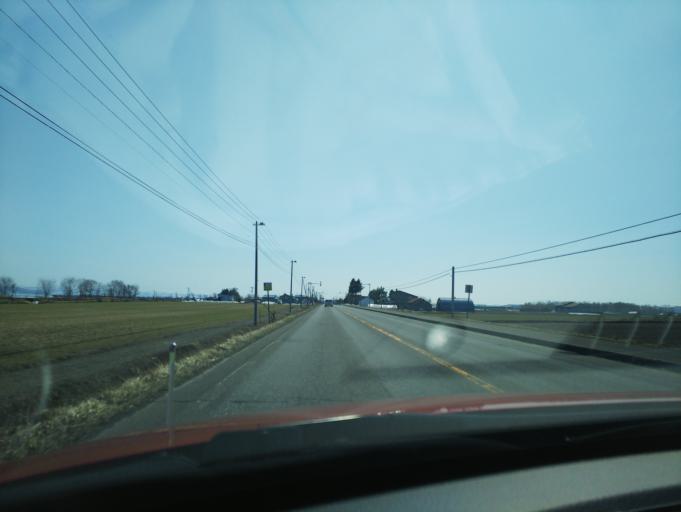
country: JP
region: Hokkaido
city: Nayoro
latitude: 44.2491
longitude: 142.3947
